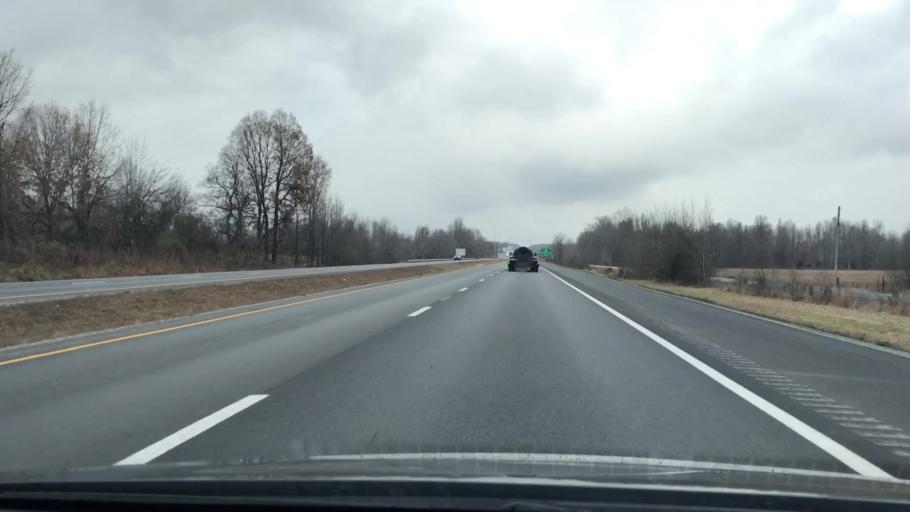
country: US
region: Kentucky
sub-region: Hopkins County
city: Nortonville
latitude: 37.2379
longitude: -87.4469
